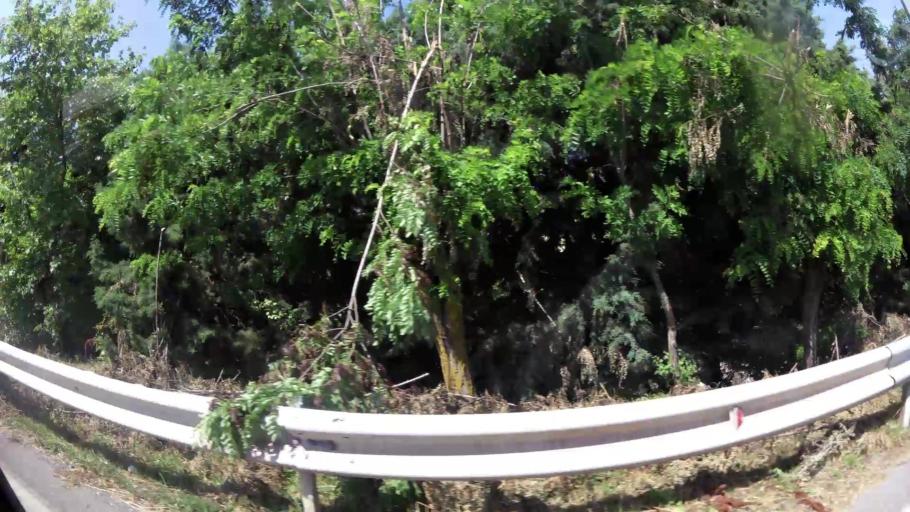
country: GR
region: West Macedonia
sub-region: Nomos Kozanis
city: Koila
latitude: 40.3162
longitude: 21.7855
